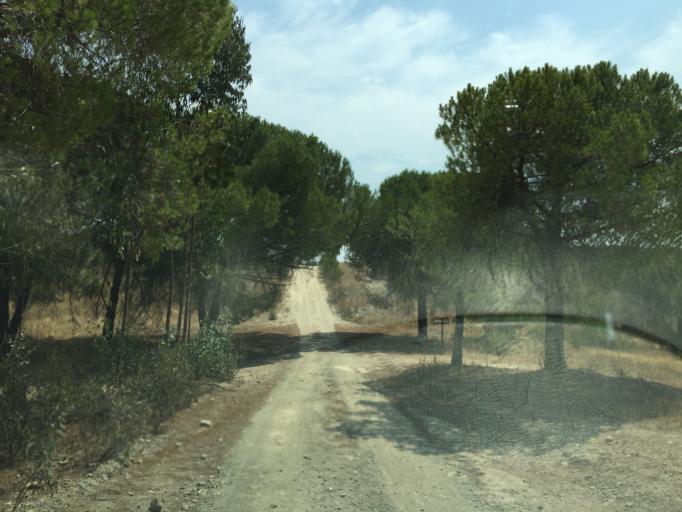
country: PT
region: Setubal
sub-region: Grandola
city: Grandola
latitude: 38.1071
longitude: -8.4904
